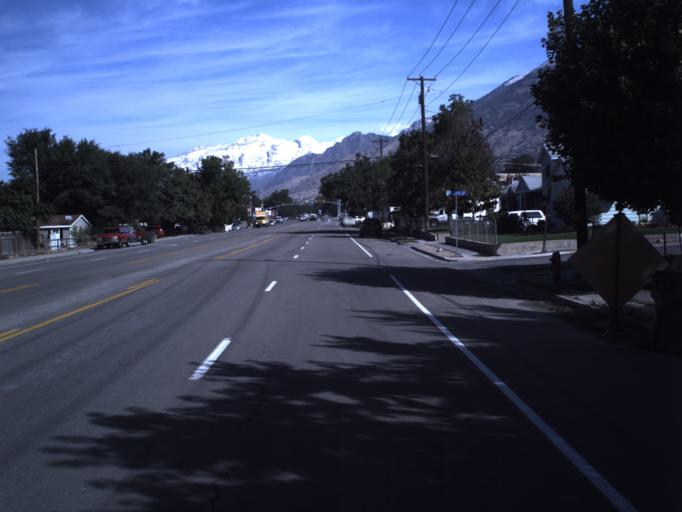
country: US
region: Utah
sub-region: Utah County
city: Pleasant Grove
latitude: 40.3558
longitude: -111.7406
